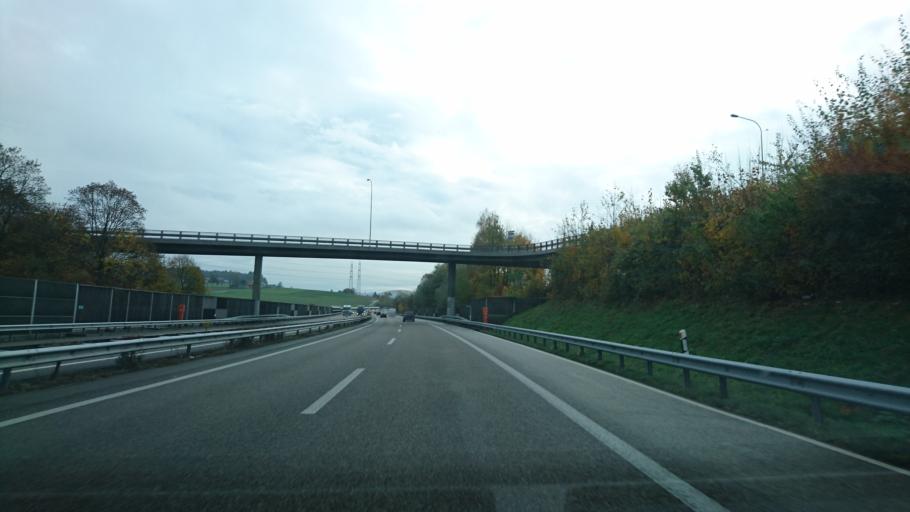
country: CH
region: Aargau
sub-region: Bezirk Zofingen
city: Safenwil
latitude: 47.3228
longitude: 7.9932
